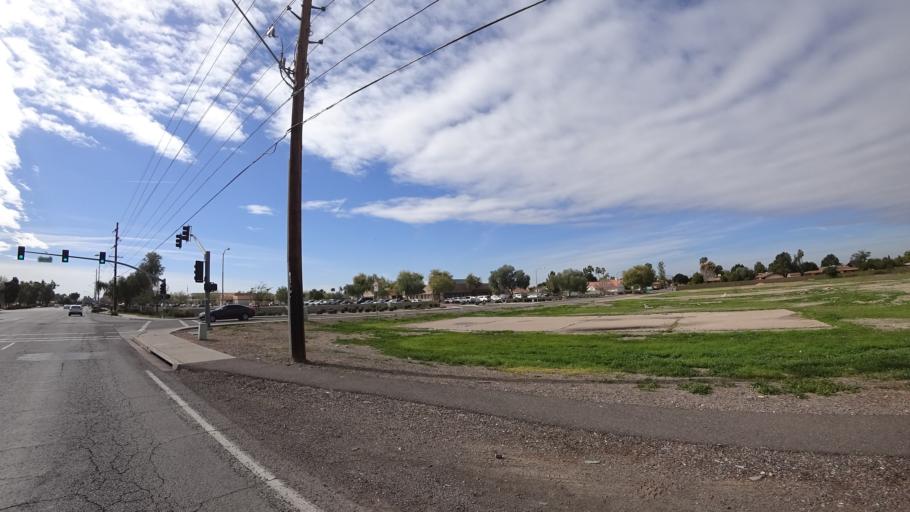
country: US
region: Arizona
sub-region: Maricopa County
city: Peoria
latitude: 33.6359
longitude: -112.1863
